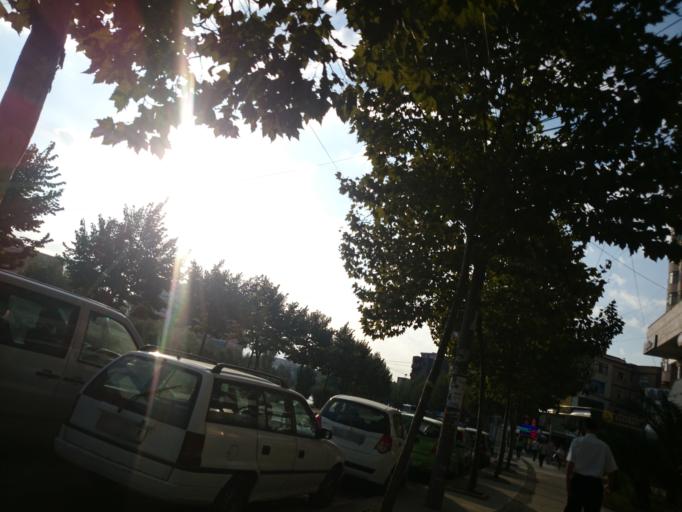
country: AL
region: Tirane
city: Tirana
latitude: 41.3216
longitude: 19.7921
